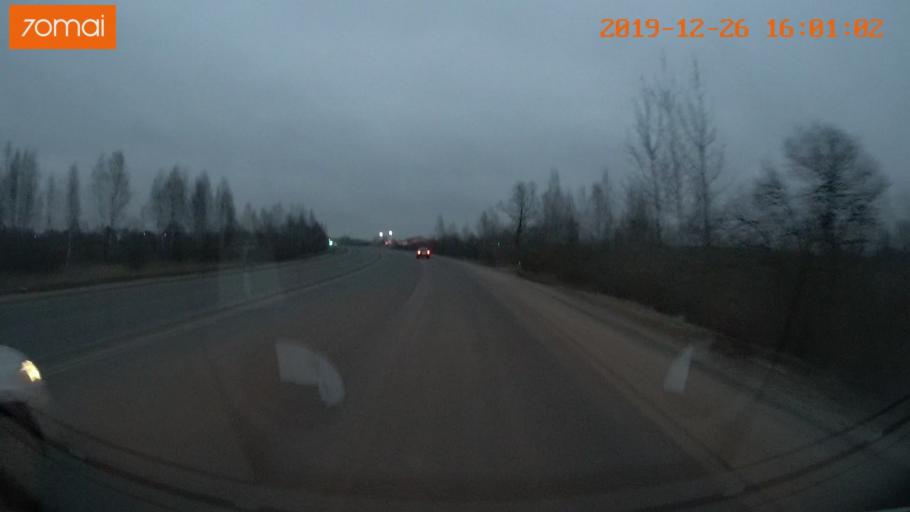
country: RU
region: Jaroslavl
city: Rybinsk
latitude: 58.0182
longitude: 38.8123
